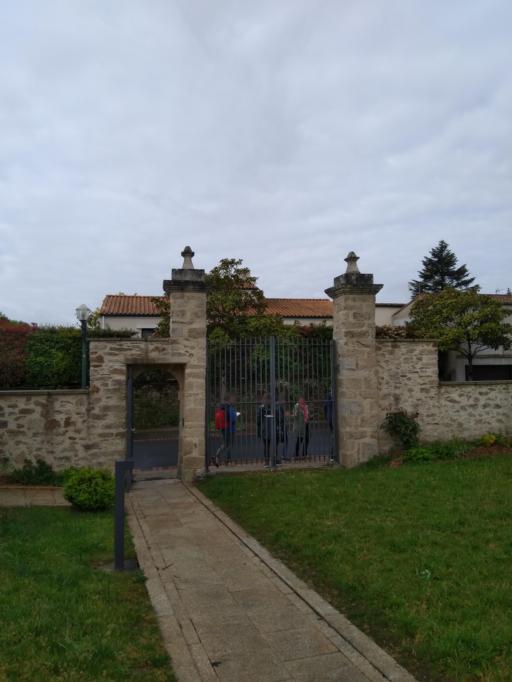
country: FR
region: Pays de la Loire
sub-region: Departement de la Loire-Atlantique
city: Saint-Fiacre-sur-Maine
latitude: 47.1257
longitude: -1.4205
